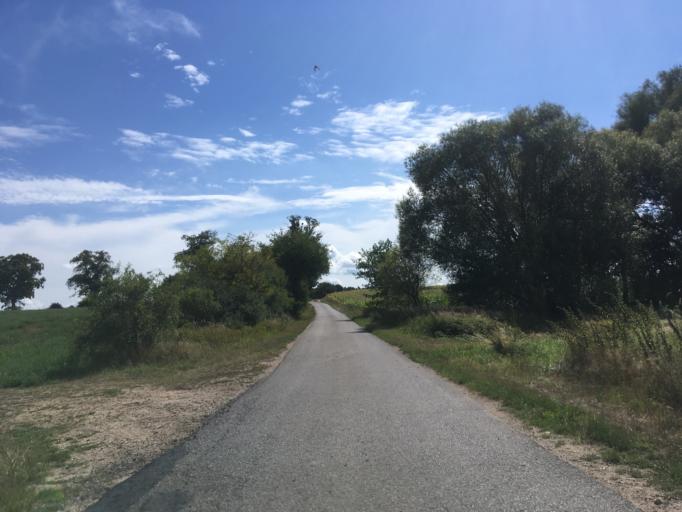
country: DE
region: Brandenburg
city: Gerswalde
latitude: 53.1591
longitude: 13.7591
